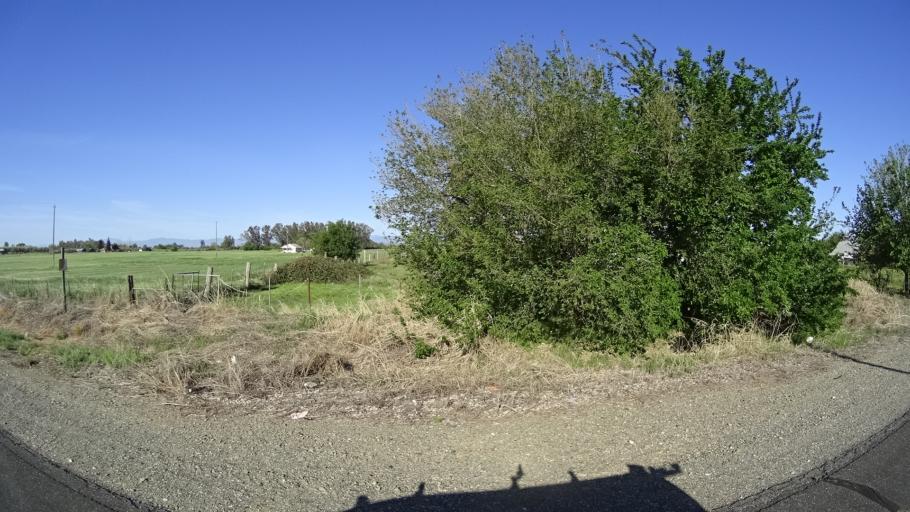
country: US
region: California
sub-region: Glenn County
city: Orland
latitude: 39.7932
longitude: -122.1974
